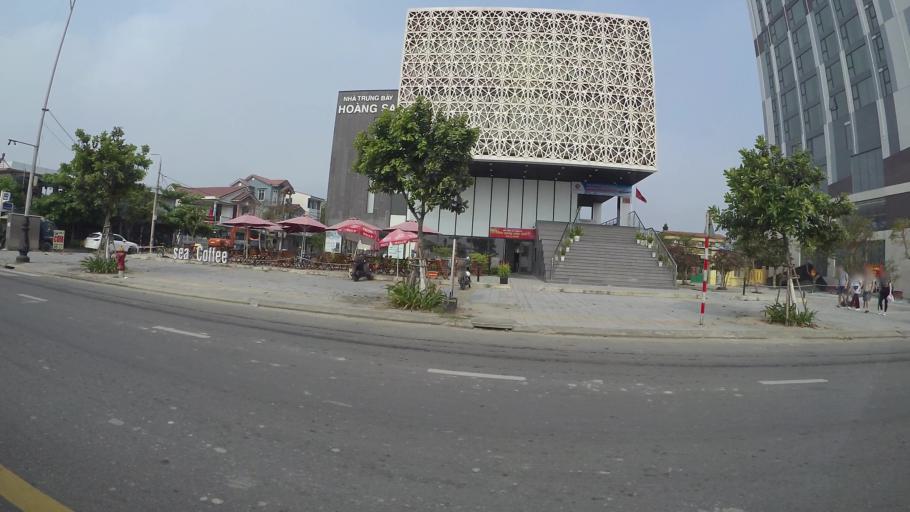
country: VN
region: Da Nang
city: Son Tra
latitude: 16.0935
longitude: 108.2515
